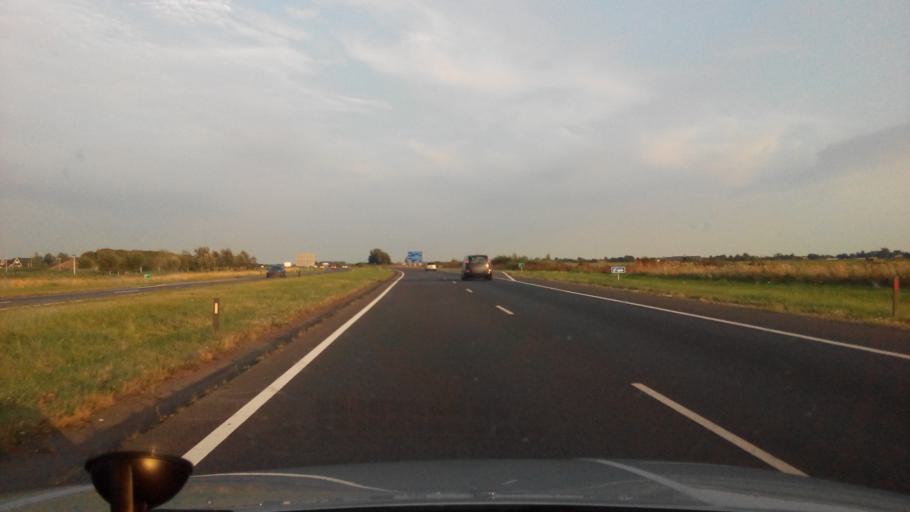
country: NL
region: South Holland
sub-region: Gemeente Alphen aan den Rijn
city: Alphen aan den Rijn
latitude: 52.1176
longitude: 4.6336
